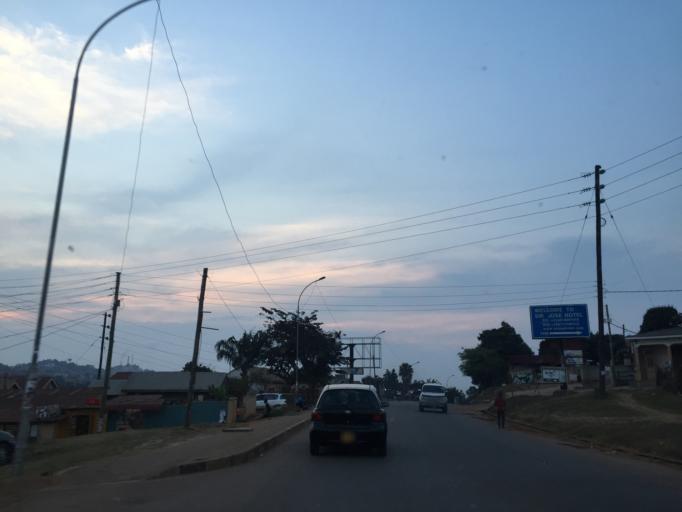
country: UG
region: Central Region
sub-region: Kampala District
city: Kampala
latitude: 0.2589
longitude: 32.6272
